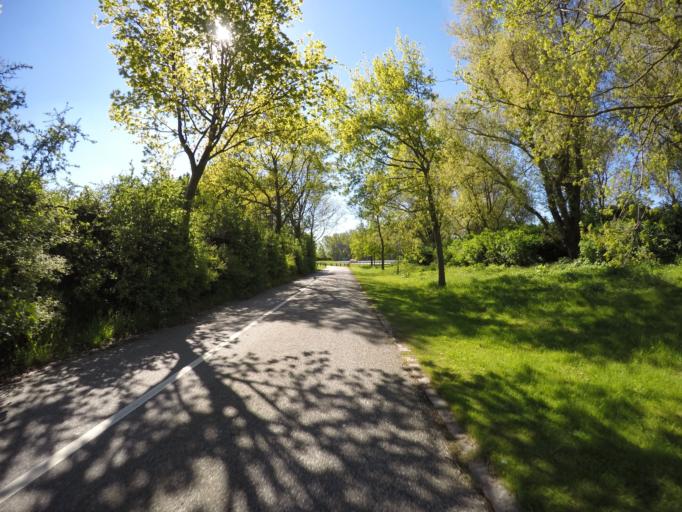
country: SE
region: Skane
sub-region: Malmo
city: Oxie
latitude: 55.5651
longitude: 13.0630
